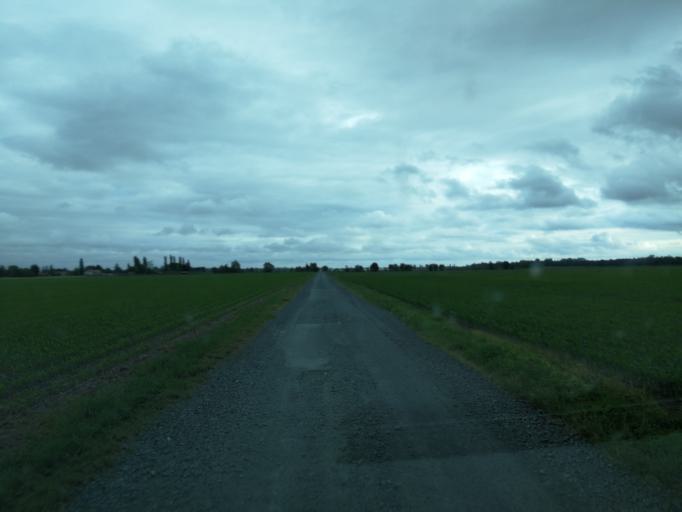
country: FR
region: Pays de la Loire
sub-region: Departement de la Vendee
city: Vix
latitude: 46.3631
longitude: -0.9357
